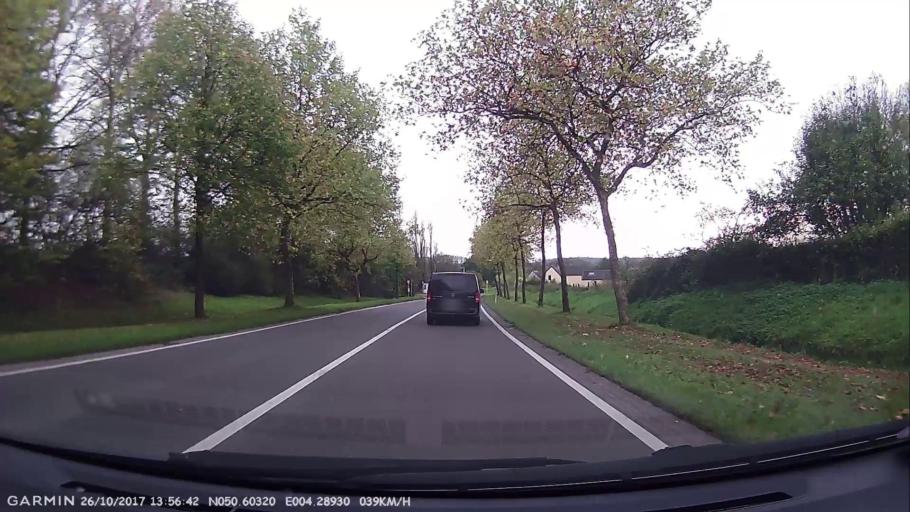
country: BE
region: Wallonia
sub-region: Province du Brabant Wallon
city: Nivelles
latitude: 50.6031
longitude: 4.2894
